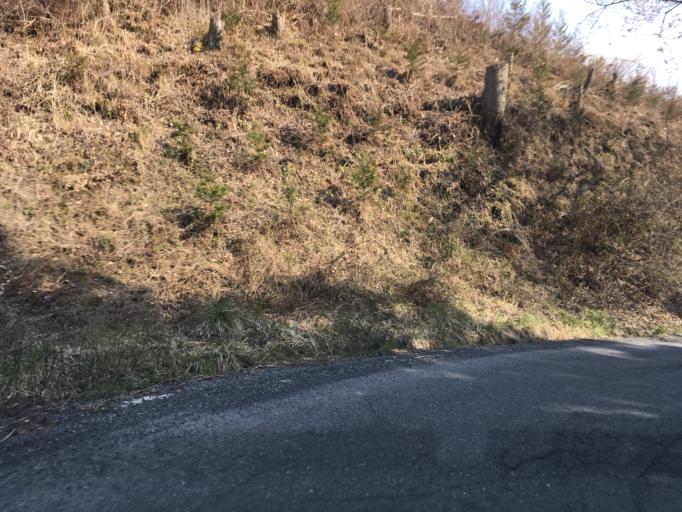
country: JP
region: Iwate
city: Ichinoseki
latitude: 38.8212
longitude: 141.3146
